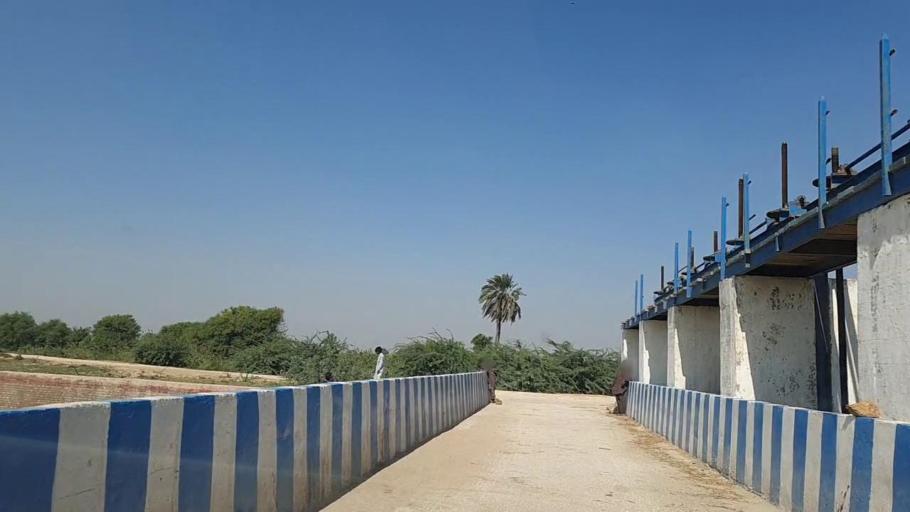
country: PK
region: Sindh
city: Daro Mehar
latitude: 24.8049
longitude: 68.1824
